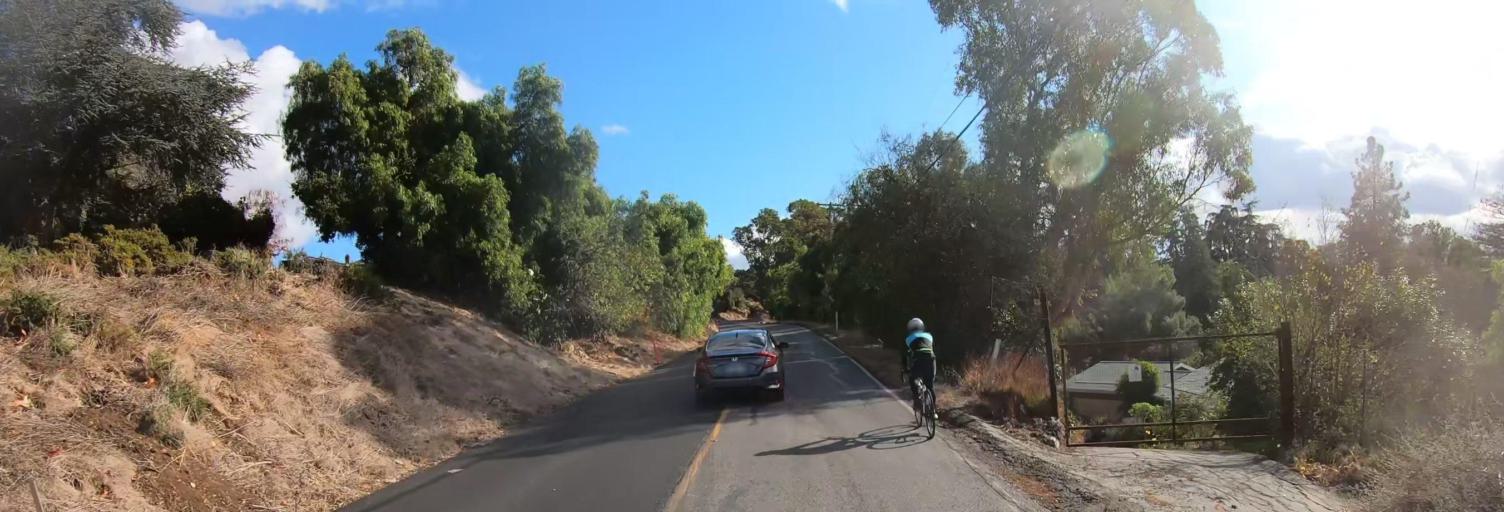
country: US
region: California
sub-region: Santa Clara County
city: East Foothills
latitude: 37.3818
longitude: -121.8127
